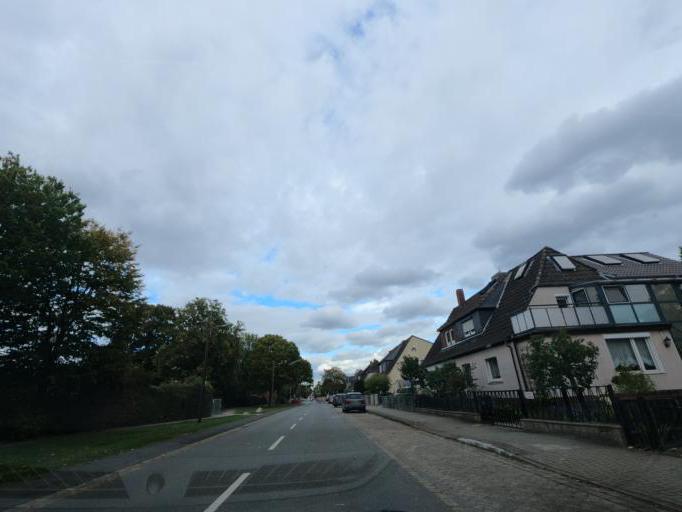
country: DE
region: Lower Saxony
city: Braunschweig
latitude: 52.2468
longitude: 10.4841
